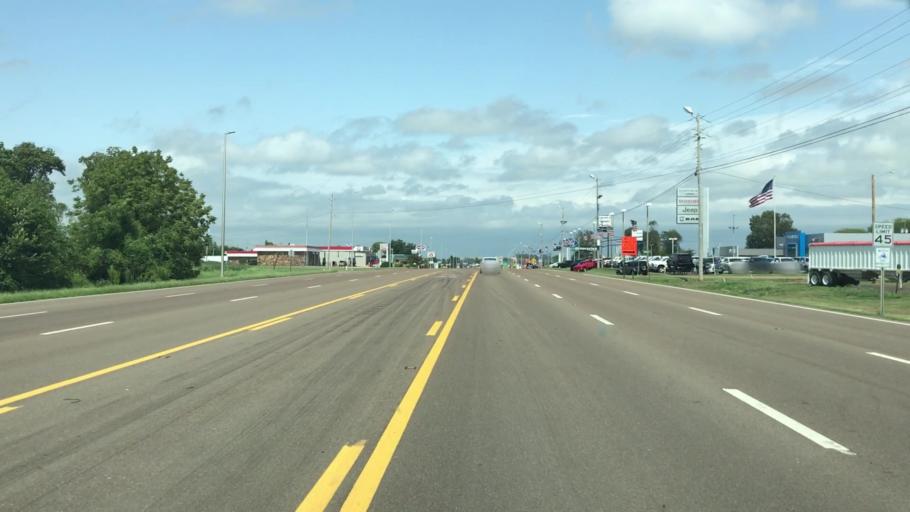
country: US
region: Tennessee
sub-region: Obion County
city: Union City
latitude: 36.4057
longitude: -89.0852
